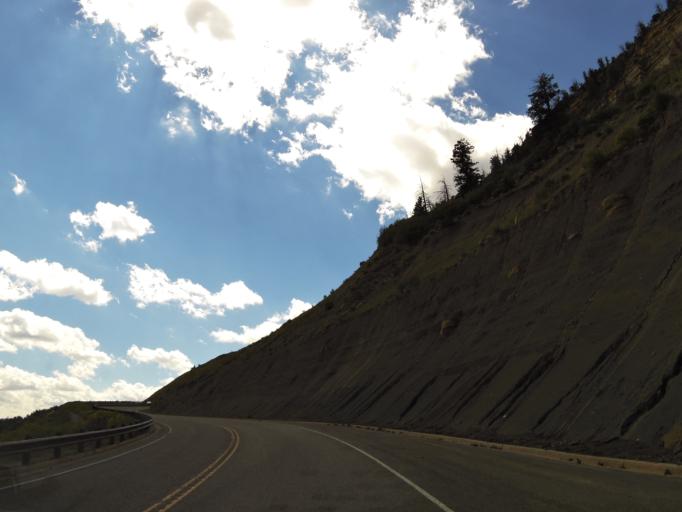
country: US
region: Colorado
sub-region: Montezuma County
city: Mancos
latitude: 37.3111
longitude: -108.4159
